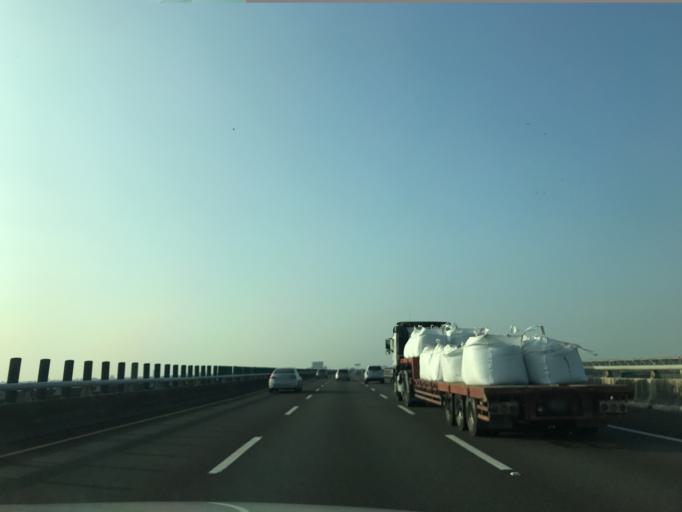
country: TW
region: Taiwan
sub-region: Yunlin
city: Douliu
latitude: 23.8087
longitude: 120.4844
